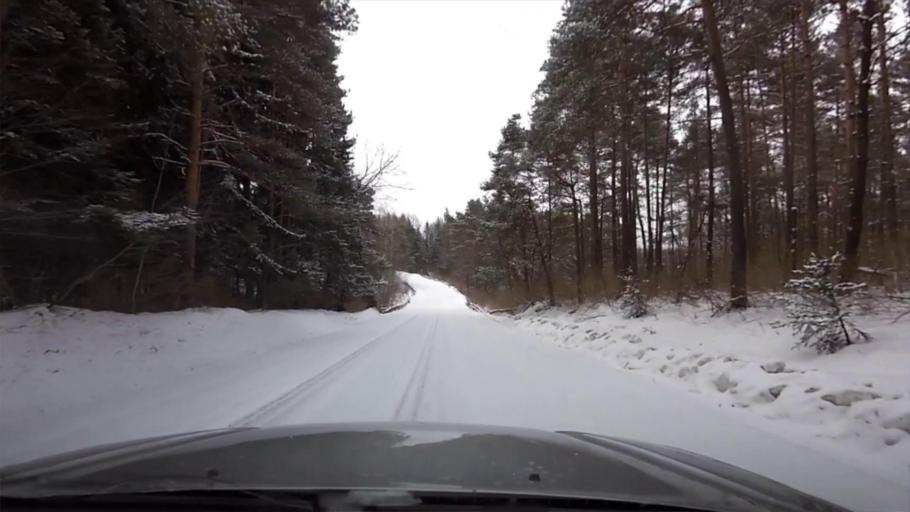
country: US
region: New York
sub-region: Cattaraugus County
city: Franklinville
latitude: 42.3393
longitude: -78.3687
